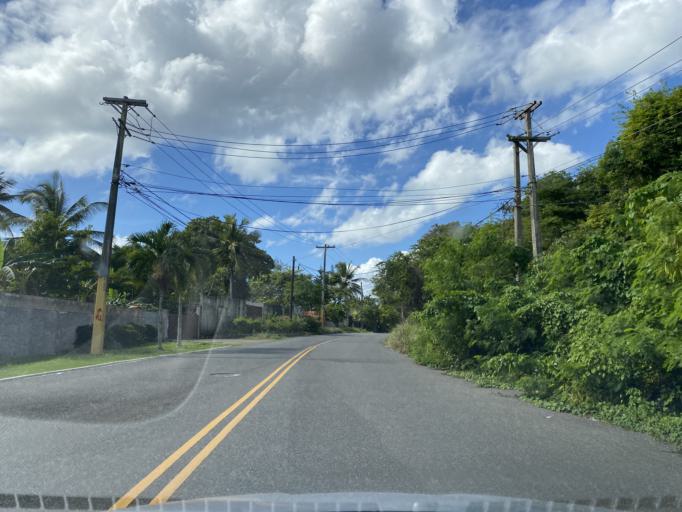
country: DO
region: Santo Domingo
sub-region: Santo Domingo
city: Boca Chica
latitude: 18.4490
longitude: -69.5981
